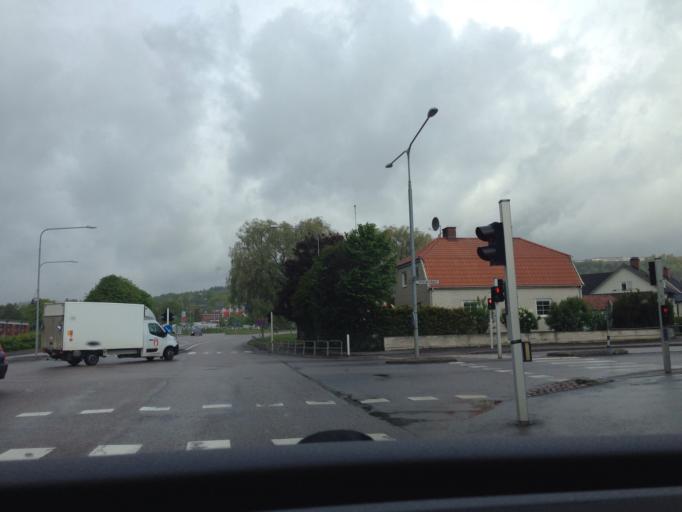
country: SE
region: Vaestra Goetaland
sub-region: Skovde Kommun
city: Skoevde
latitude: 58.3951
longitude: 13.8424
